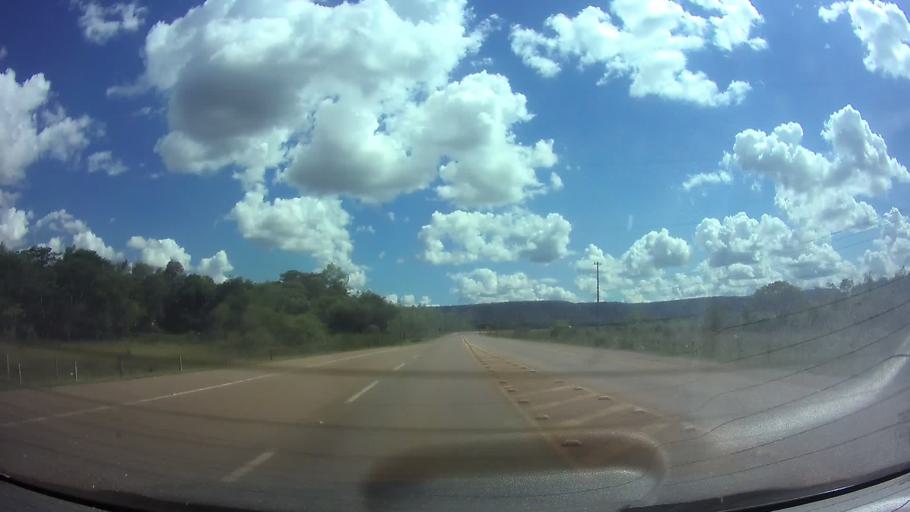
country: PY
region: Guaira
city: Itape
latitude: -25.9103
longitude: -56.6759
